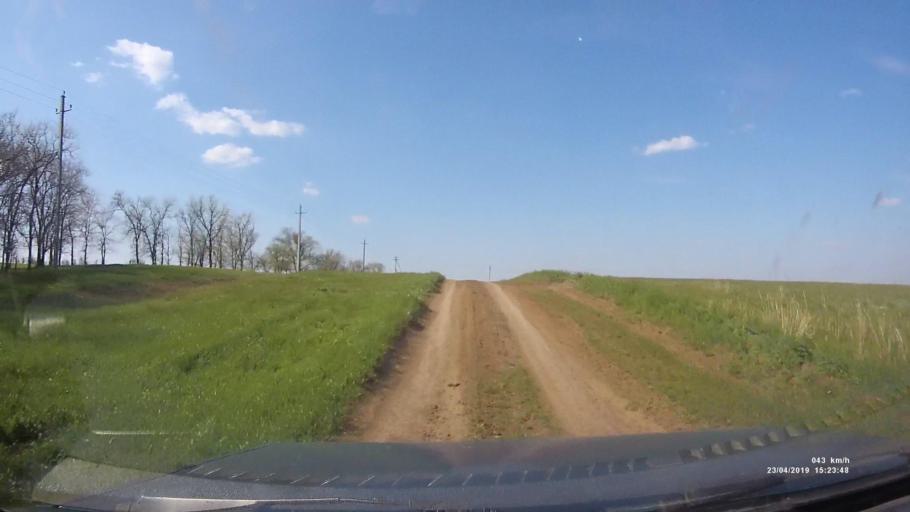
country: RU
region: Rostov
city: Remontnoye
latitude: 46.5378
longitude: 42.9697
